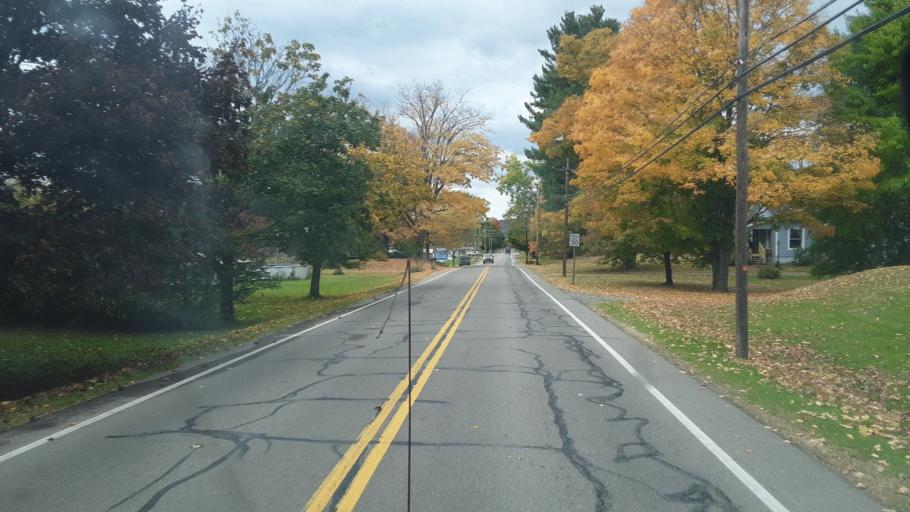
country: US
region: New York
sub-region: Allegany County
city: Belmont
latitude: 42.3031
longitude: -78.0050
